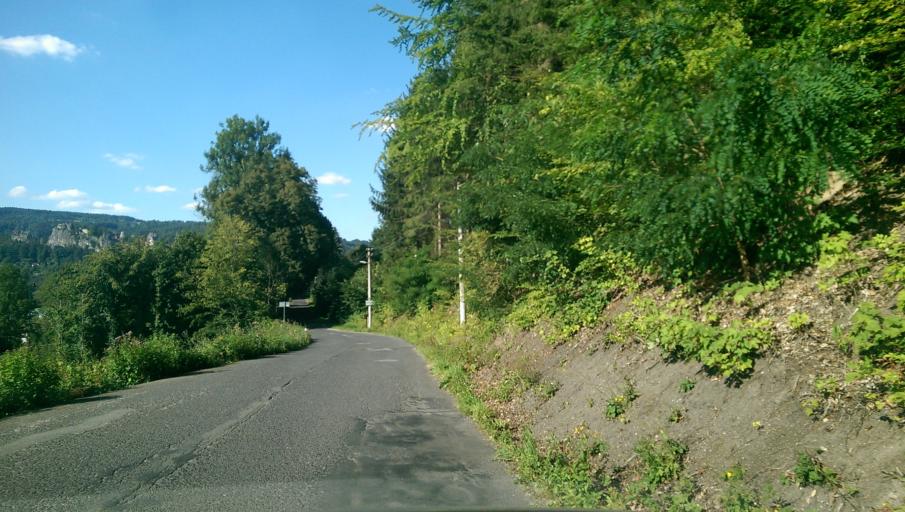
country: CZ
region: Liberecky
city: Mala Skala
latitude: 50.6301
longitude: 15.1919
